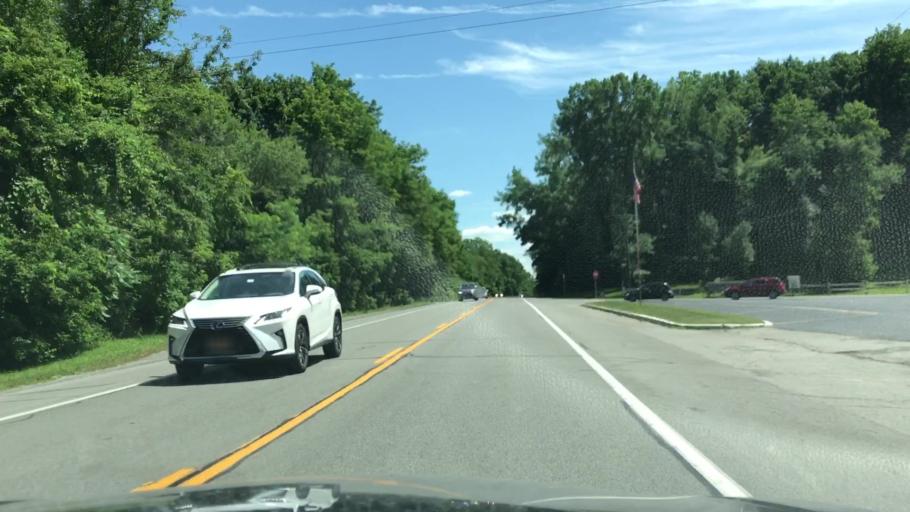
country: US
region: New York
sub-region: Livingston County
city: Mount Morris
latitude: 42.7535
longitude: -77.8840
